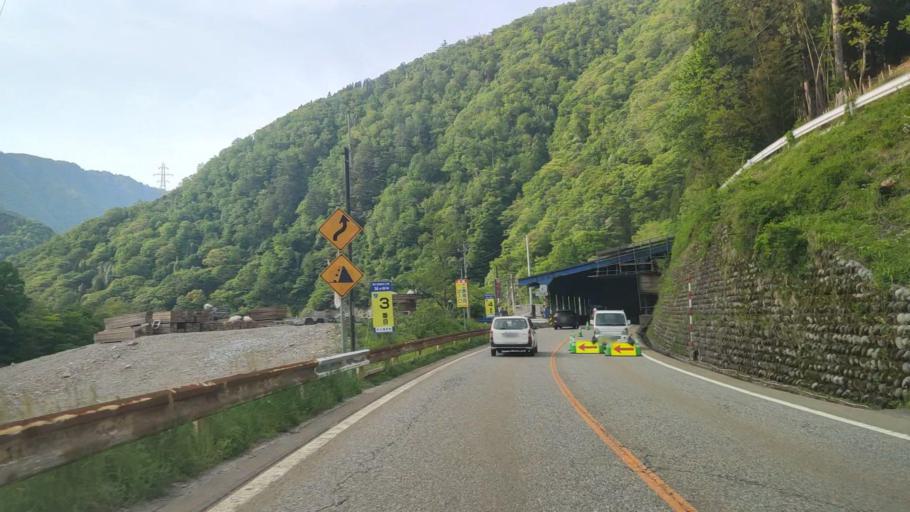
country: JP
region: Gifu
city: Takayama
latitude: 36.3690
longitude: 137.2826
